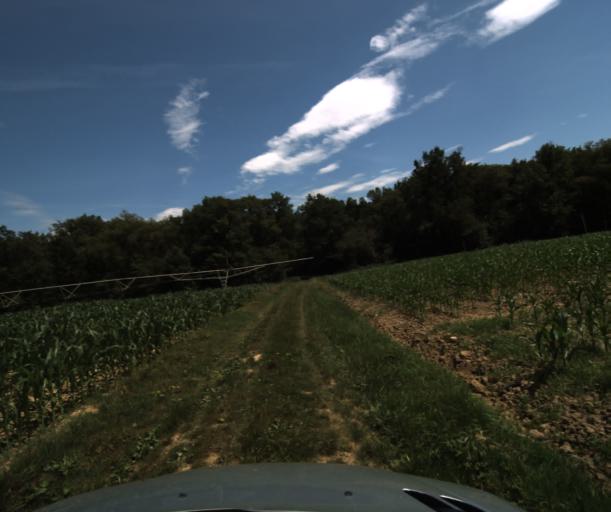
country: FR
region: Midi-Pyrenees
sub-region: Departement de la Haute-Garonne
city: Labastidette
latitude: 43.4637
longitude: 1.2259
